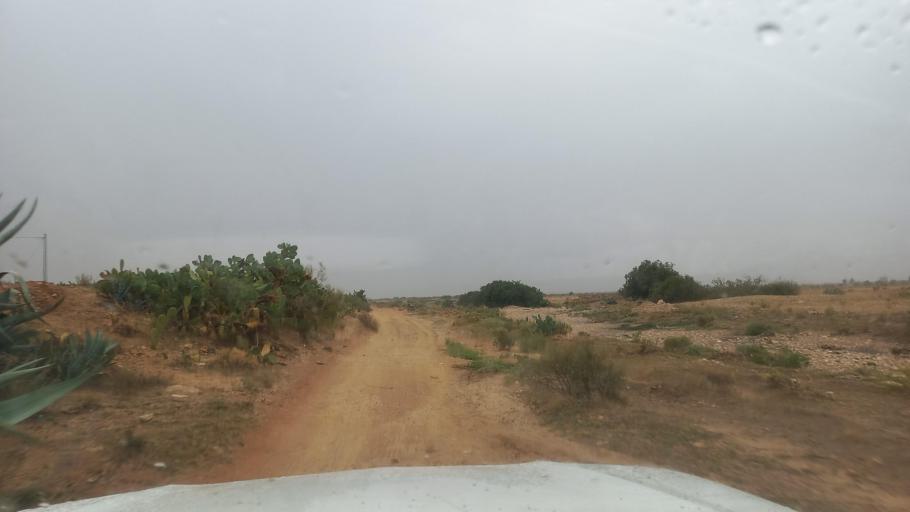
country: TN
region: Al Qasrayn
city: Kasserine
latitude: 35.2702
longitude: 8.9457
